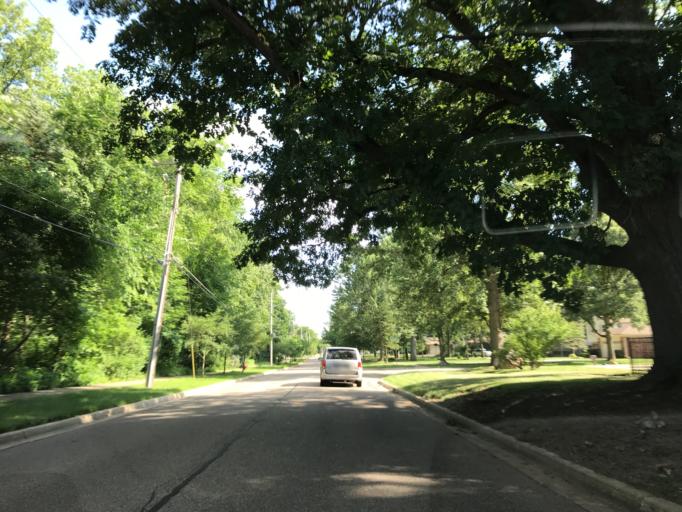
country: US
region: Michigan
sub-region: Oakland County
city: Farmington
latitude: 42.4213
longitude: -83.3943
